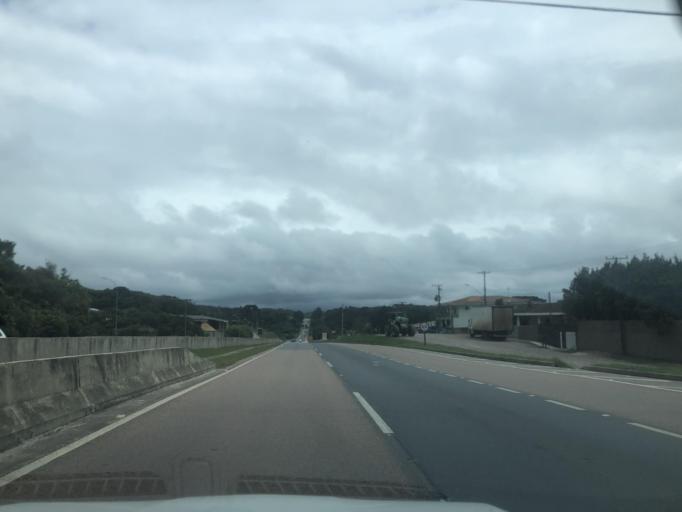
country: BR
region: Parana
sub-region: Araucaria
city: Araucaria
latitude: -25.7823
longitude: -49.3256
